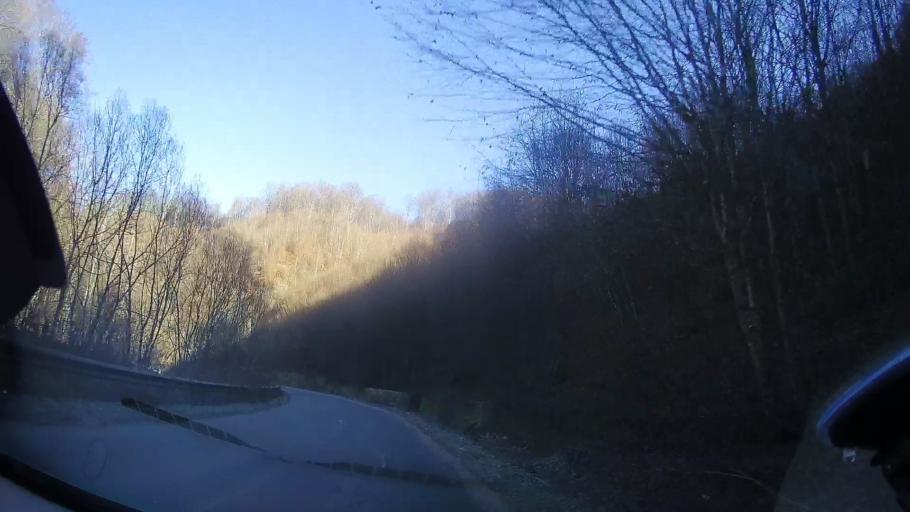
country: RO
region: Cluj
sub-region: Comuna Sacueu
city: Sacuieu
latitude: 46.8396
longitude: 22.8624
